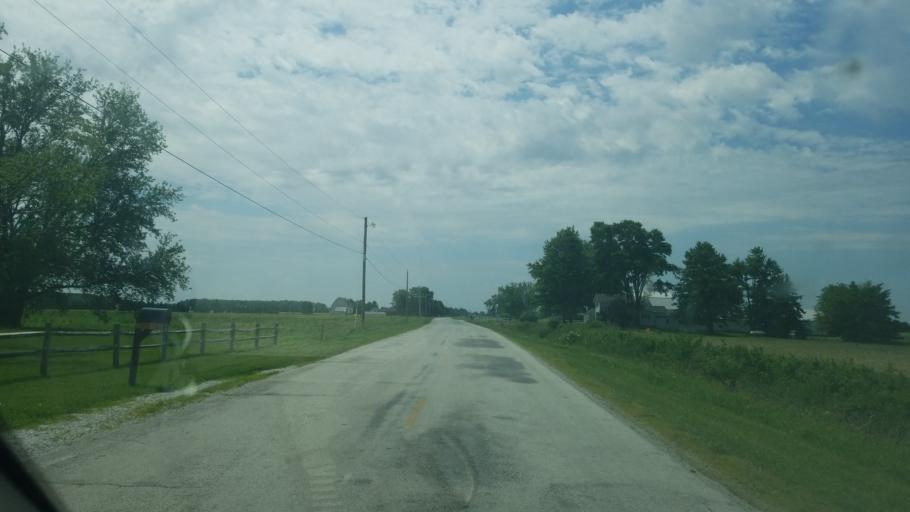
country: US
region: Ohio
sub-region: Wood County
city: Bowling Green
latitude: 41.2931
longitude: -83.5927
